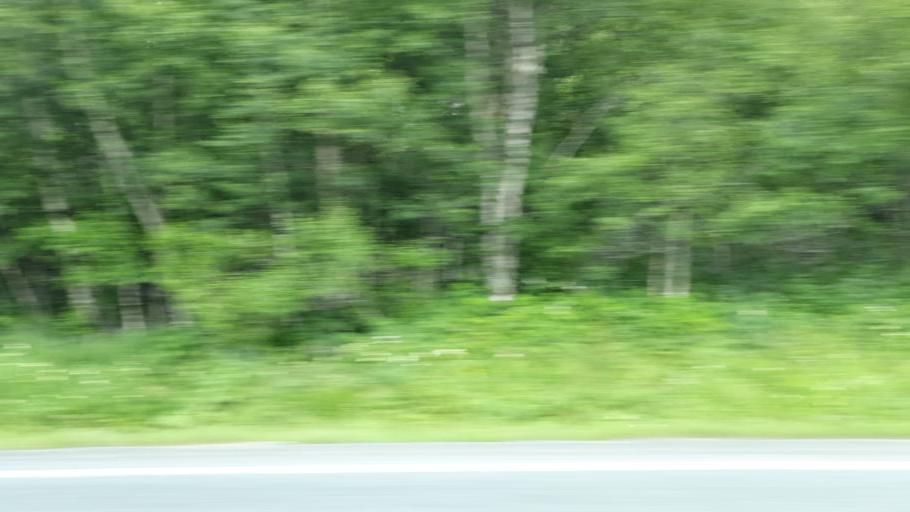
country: NO
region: Sor-Trondelag
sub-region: Rennebu
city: Berkak
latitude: 62.8623
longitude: 10.0218
